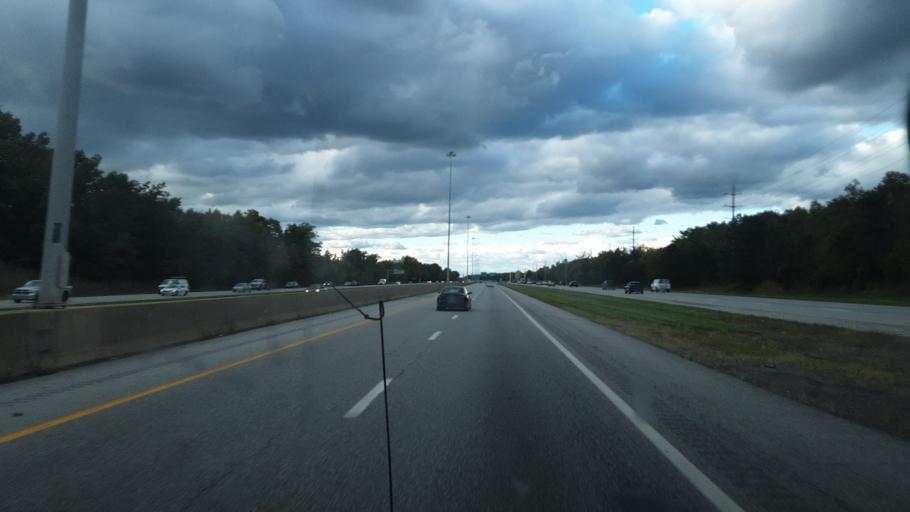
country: US
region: Ohio
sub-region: Cuyahoga County
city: Mayfield
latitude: 41.5522
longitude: -81.4482
